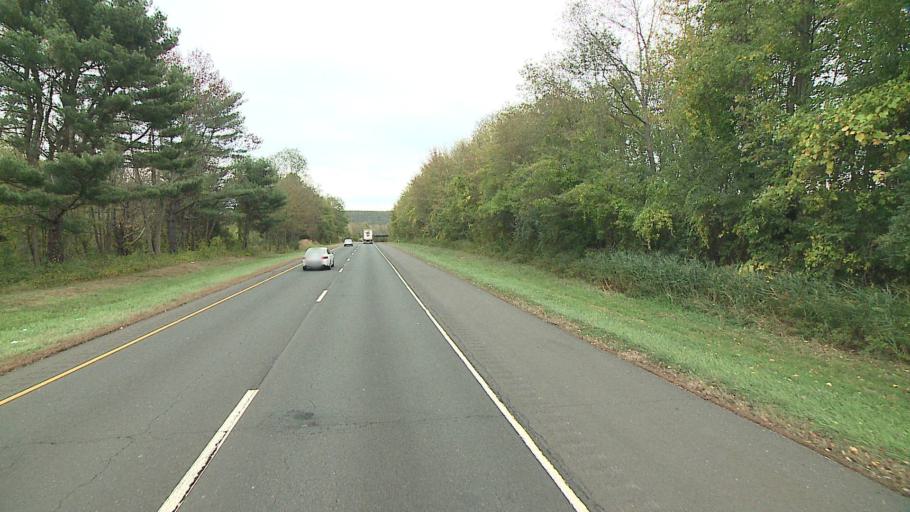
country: US
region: Connecticut
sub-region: Middlesex County
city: Higganum
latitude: 41.4990
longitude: -72.5757
